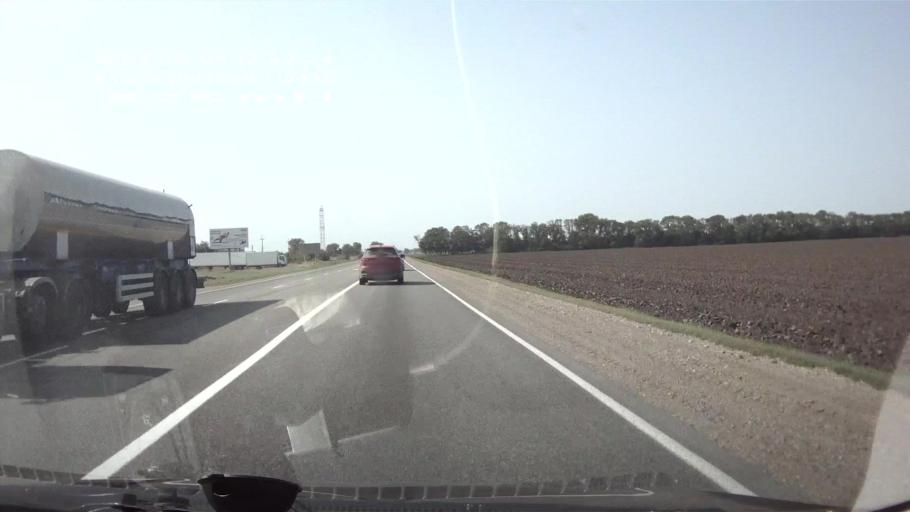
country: RU
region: Krasnodarskiy
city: Ust'-Labinsk
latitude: 45.2440
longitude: 39.7135
